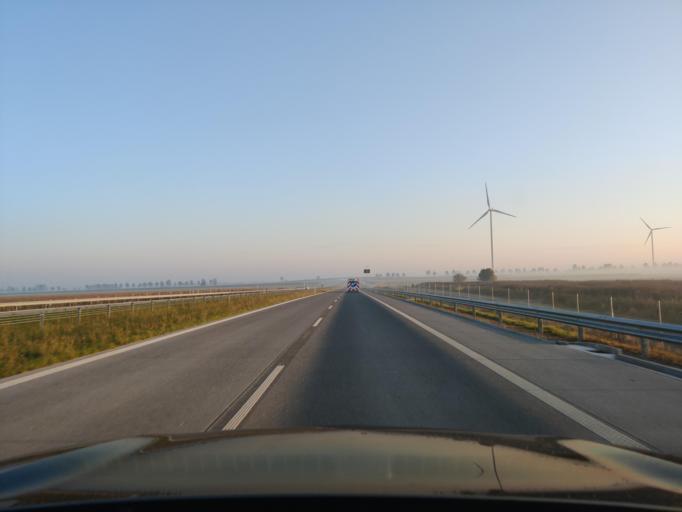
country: PL
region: Masovian Voivodeship
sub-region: Powiat mlawski
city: Wisniewo
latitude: 53.0501
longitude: 20.3613
